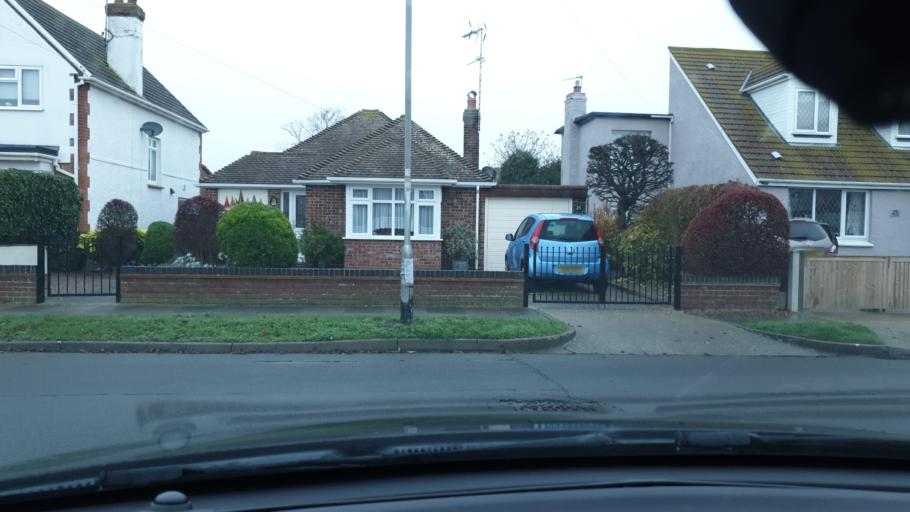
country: GB
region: England
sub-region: Essex
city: Clacton-on-Sea
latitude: 51.7986
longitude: 1.1797
